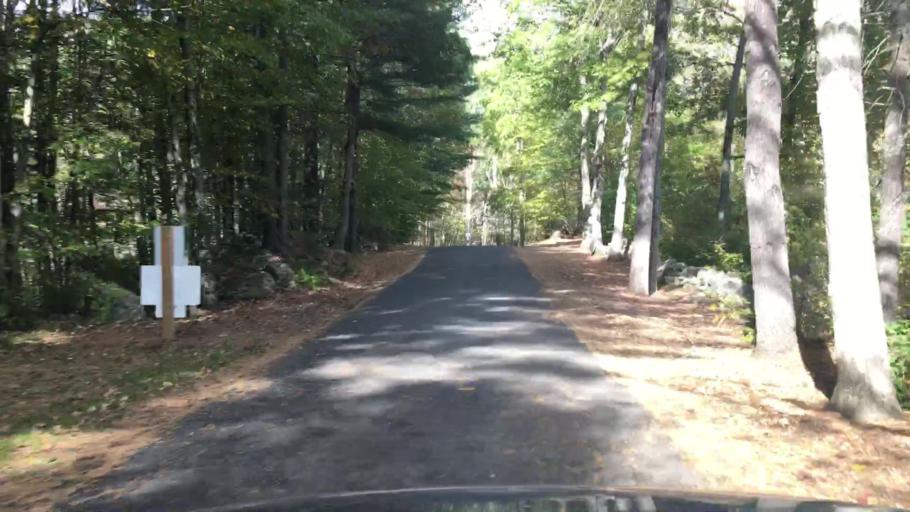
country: US
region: Connecticut
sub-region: Tolland County
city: Storrs
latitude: 41.8922
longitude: -72.1757
